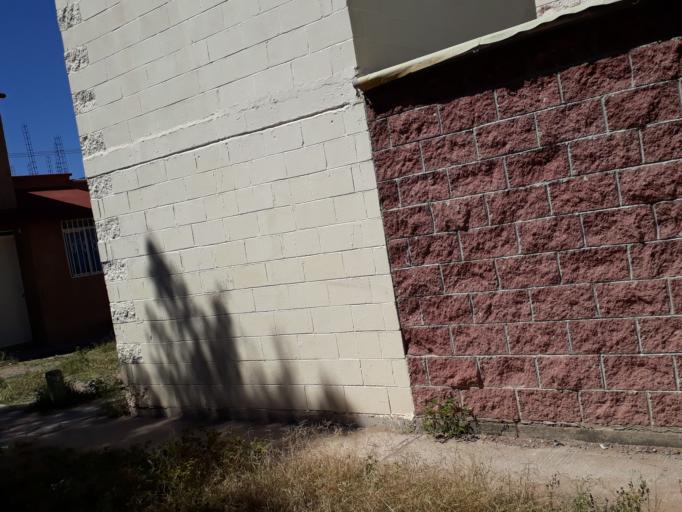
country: MX
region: Aguascalientes
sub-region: Aguascalientes
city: Cumbres III
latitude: 21.8742
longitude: -102.2347
